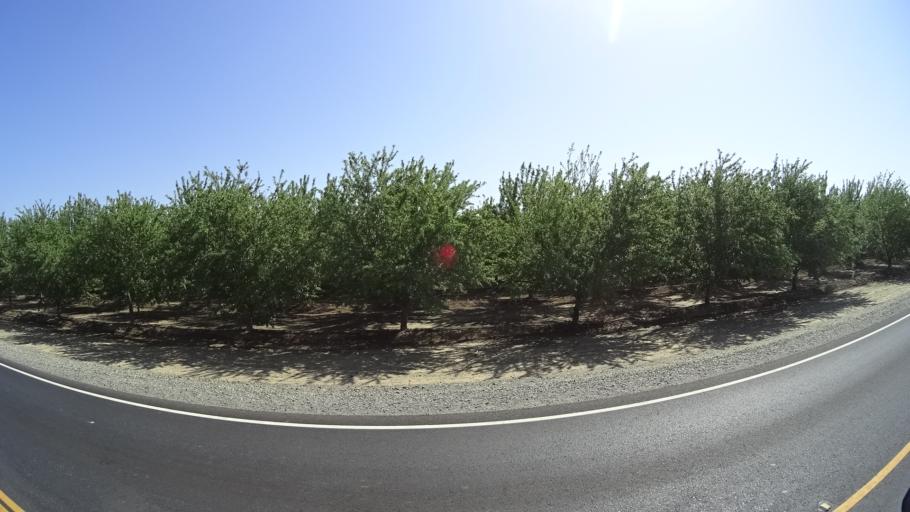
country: US
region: California
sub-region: Glenn County
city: Hamilton City
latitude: 39.6374
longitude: -122.0650
